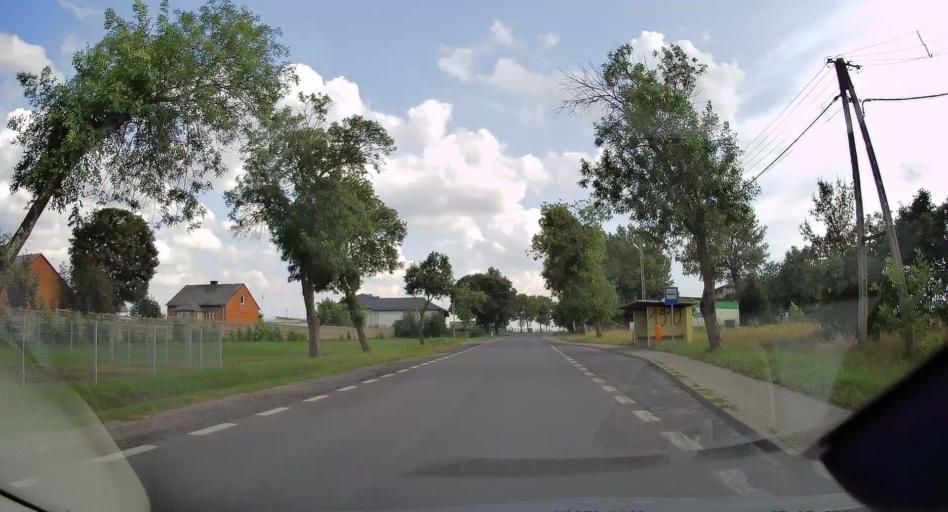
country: PL
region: Lodz Voivodeship
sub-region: Powiat tomaszowski
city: Rzeczyca
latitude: 51.6282
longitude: 20.2922
